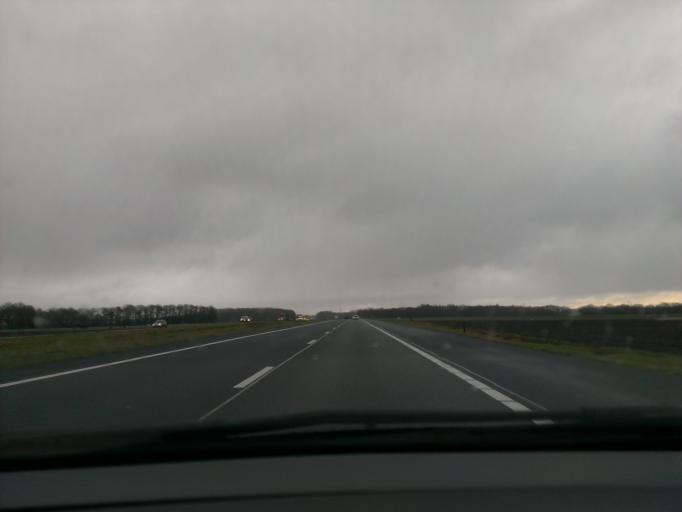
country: NL
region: Drenthe
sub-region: Gemeente Coevorden
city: Dalen
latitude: 52.7223
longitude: 6.6744
